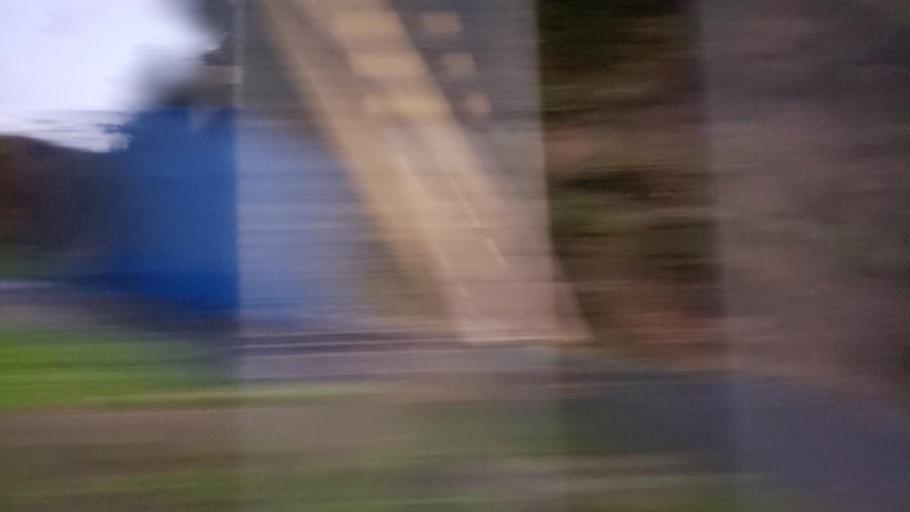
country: JP
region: Tokushima
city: Kamojimacho-jogejima
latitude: 34.0922
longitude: 134.2843
